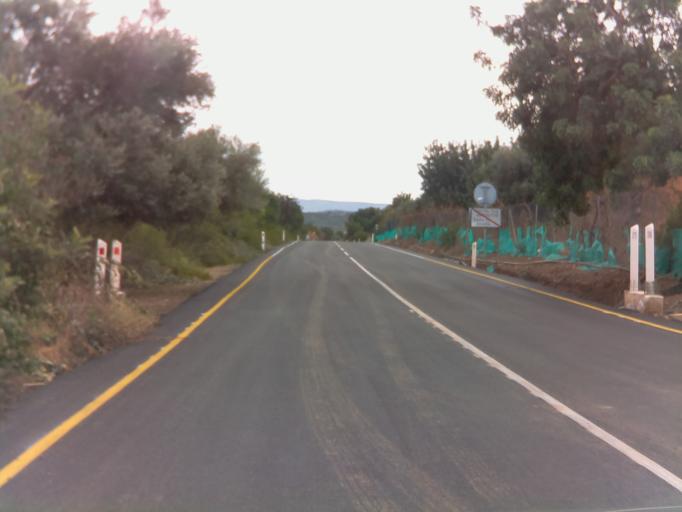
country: CY
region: Pafos
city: Polis
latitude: 35.0535
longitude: 32.3485
